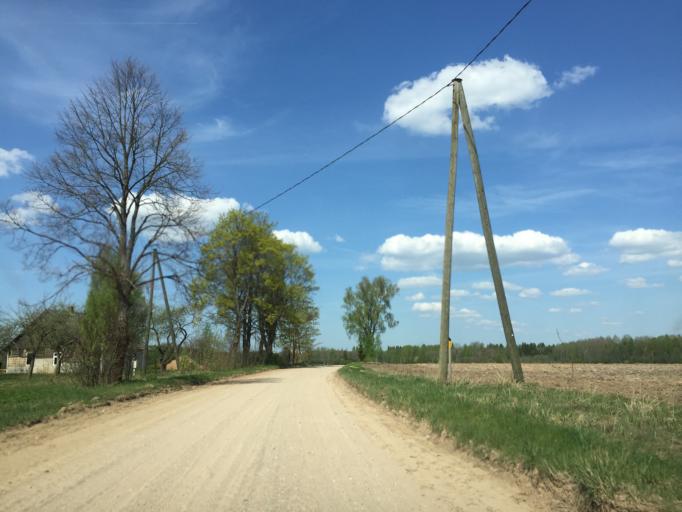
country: LV
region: Limbazu Rajons
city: Limbazi
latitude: 57.3533
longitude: 24.6478
